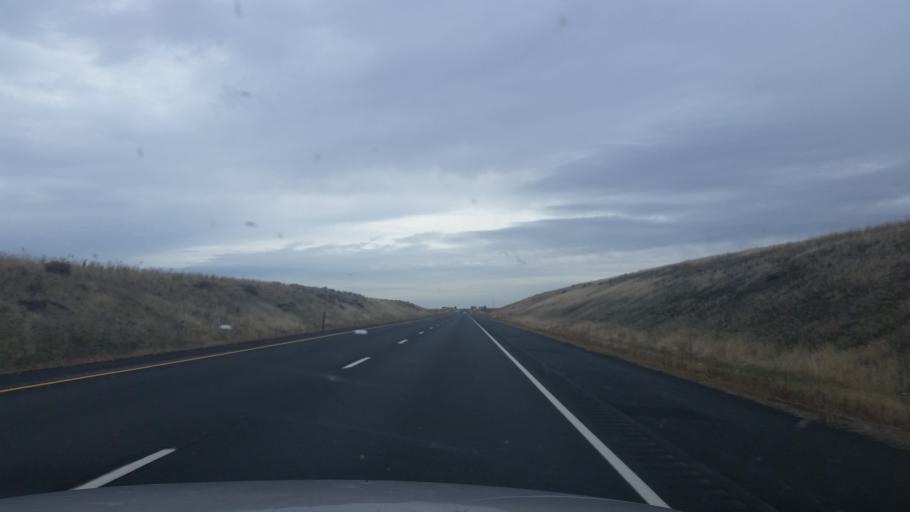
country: US
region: Washington
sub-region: Grant County
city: Warden
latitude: 47.0864
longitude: -118.7828
